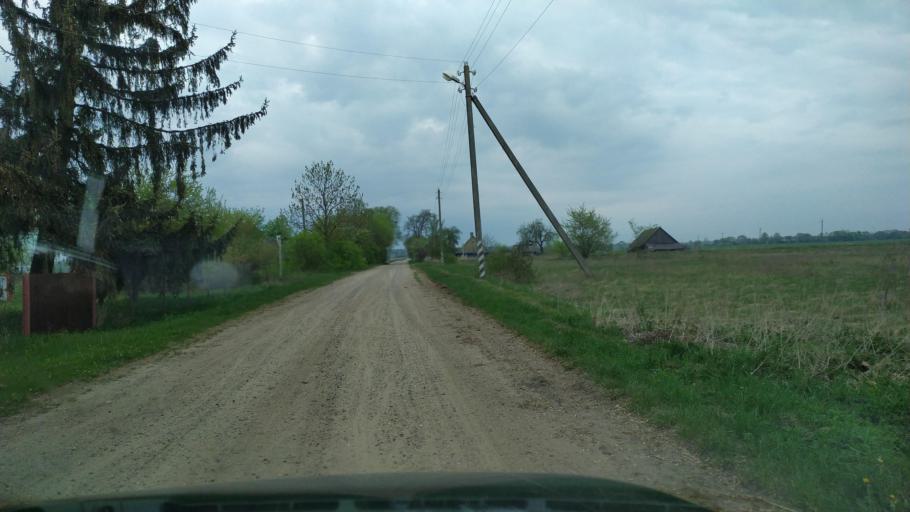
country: BY
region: Brest
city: Zhabinka
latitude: 52.1280
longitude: 24.0906
